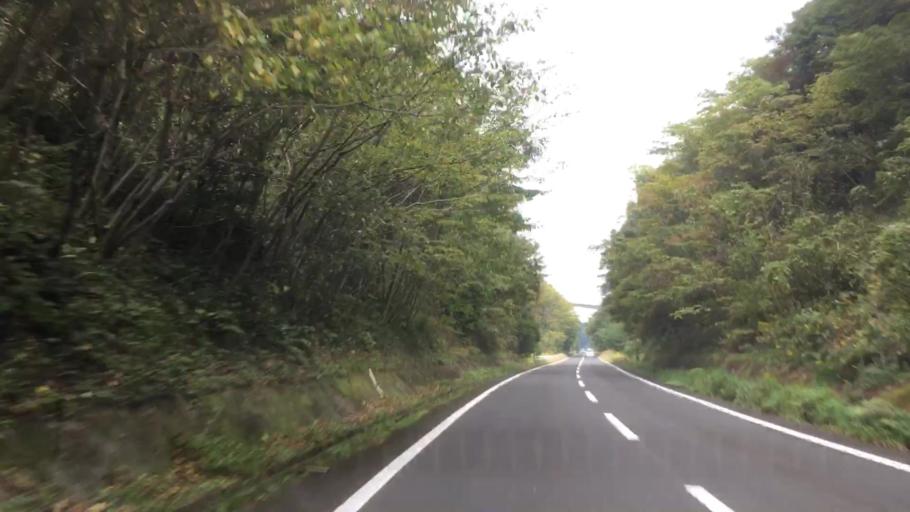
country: JP
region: Nagasaki
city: Sasebo
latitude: 32.9997
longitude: 129.7075
